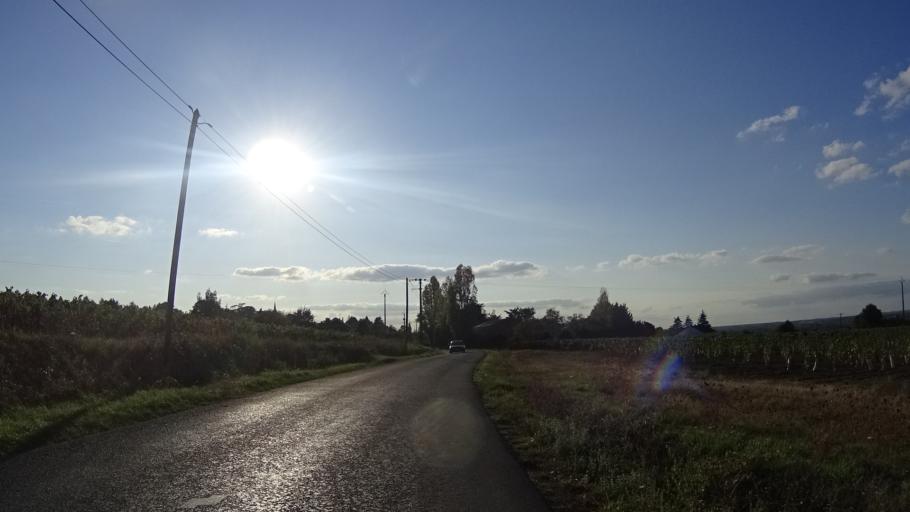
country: FR
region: Pays de la Loire
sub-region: Departement de Maine-et-Loire
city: Bouzille
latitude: 47.3404
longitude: -1.0997
